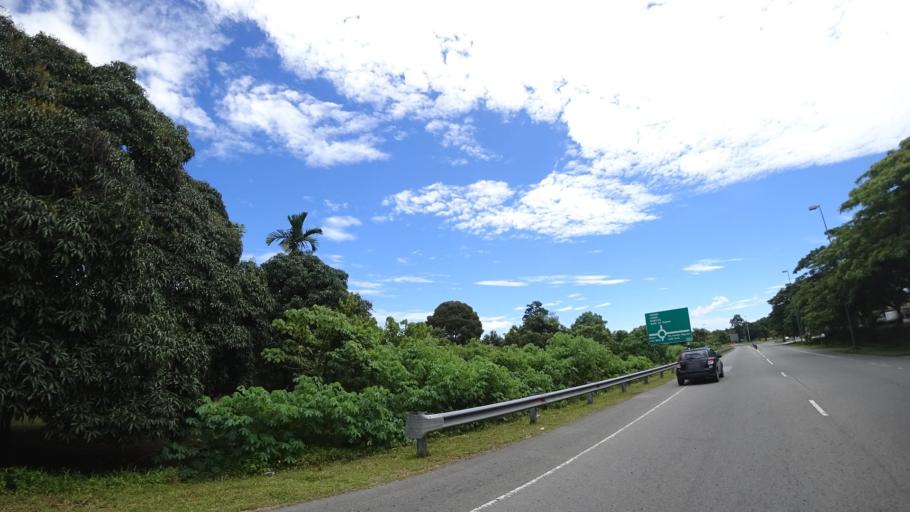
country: BN
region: Tutong
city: Tutong
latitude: 4.7685
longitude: 114.8216
